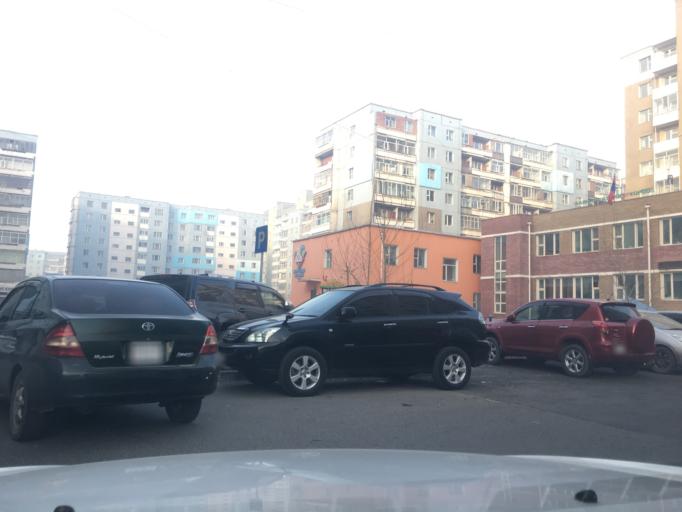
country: MN
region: Ulaanbaatar
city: Ulaanbaatar
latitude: 47.9147
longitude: 106.8689
